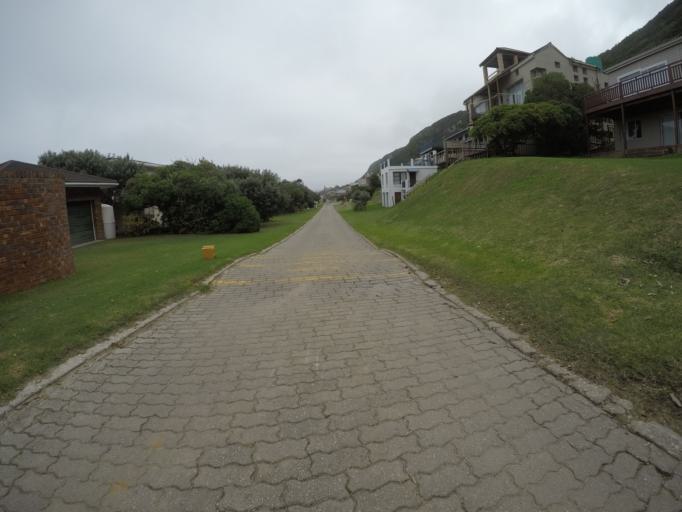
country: ZA
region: Eastern Cape
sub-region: Cacadu District Municipality
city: Kareedouw
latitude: -34.0712
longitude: 24.2190
